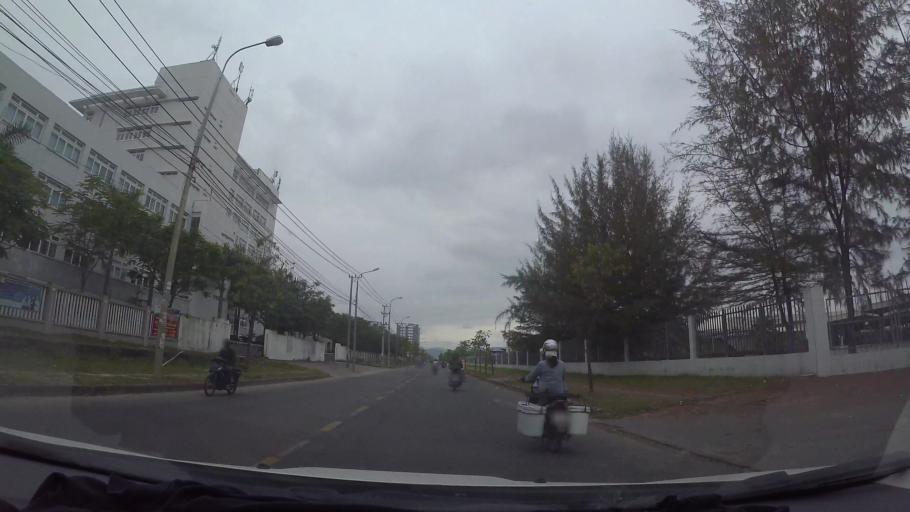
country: VN
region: Da Nang
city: Lien Chieu
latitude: 16.0726
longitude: 108.1401
